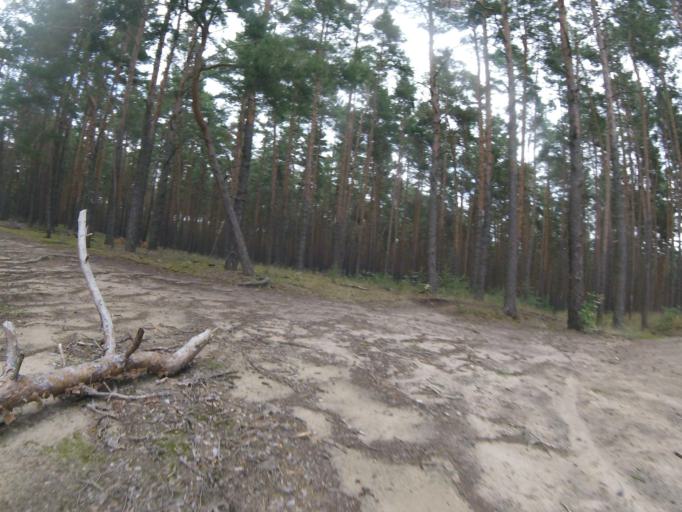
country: DE
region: Brandenburg
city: Gross Koris
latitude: 52.2057
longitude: 13.6587
